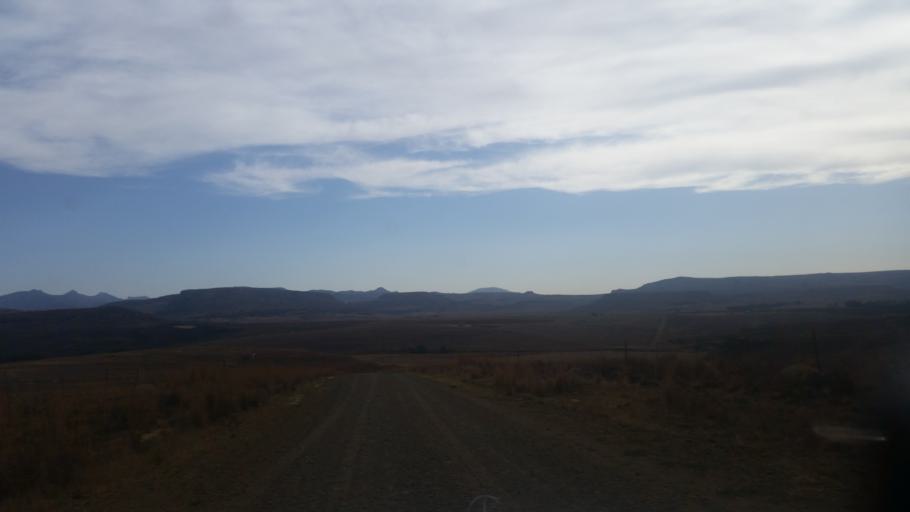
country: ZA
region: Orange Free State
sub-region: Thabo Mofutsanyana District Municipality
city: Phuthaditjhaba
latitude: -28.4007
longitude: 28.7693
